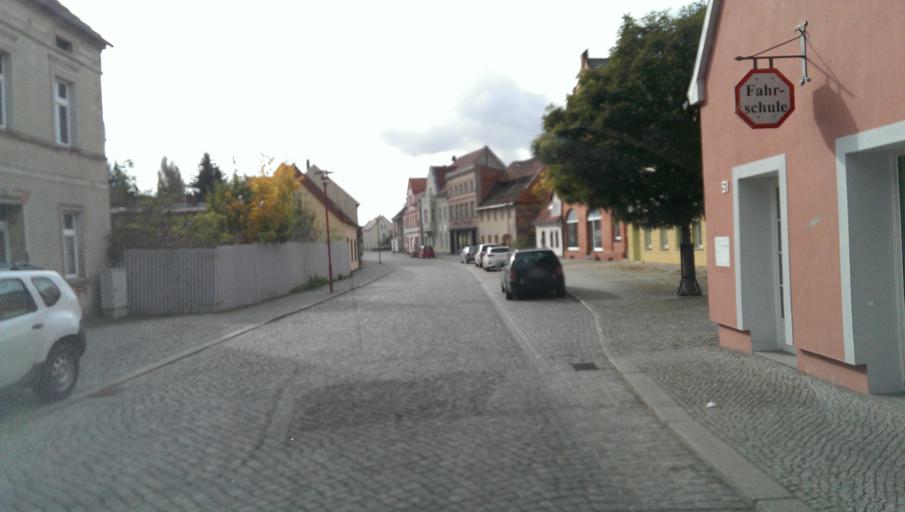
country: DE
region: Brandenburg
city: Doberlug-Kirchhain
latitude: 51.6356
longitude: 13.5611
